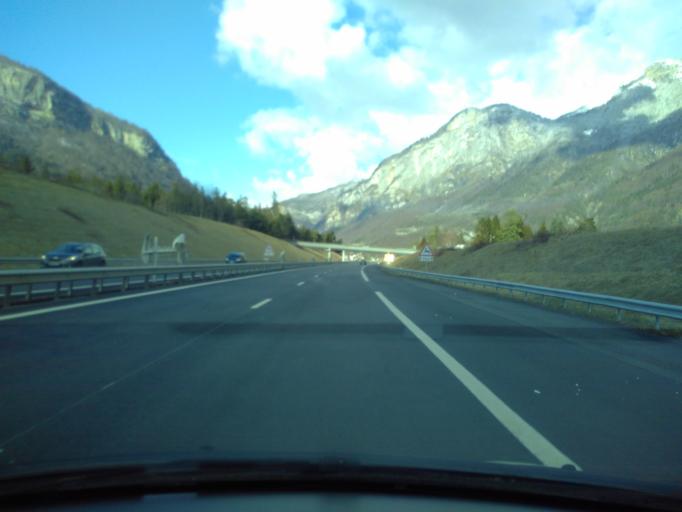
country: FR
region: Rhone-Alpes
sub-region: Departement de la Haute-Savoie
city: Sallanches
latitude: 45.9701
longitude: 6.6277
